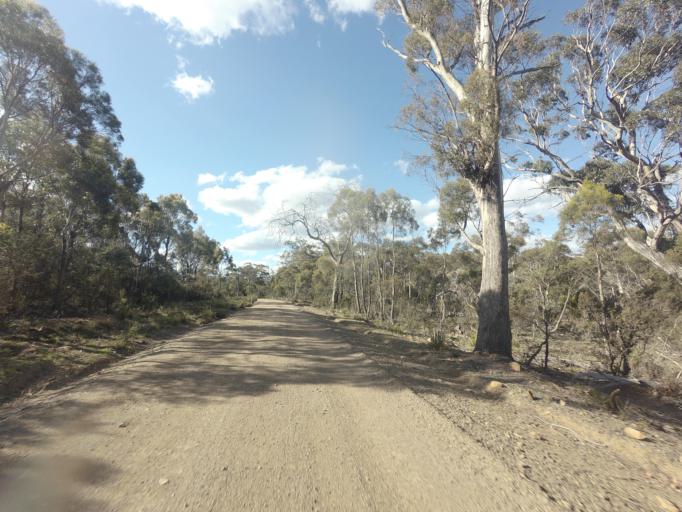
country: AU
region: Tasmania
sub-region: Break O'Day
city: St Helens
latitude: -41.8348
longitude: 148.0170
